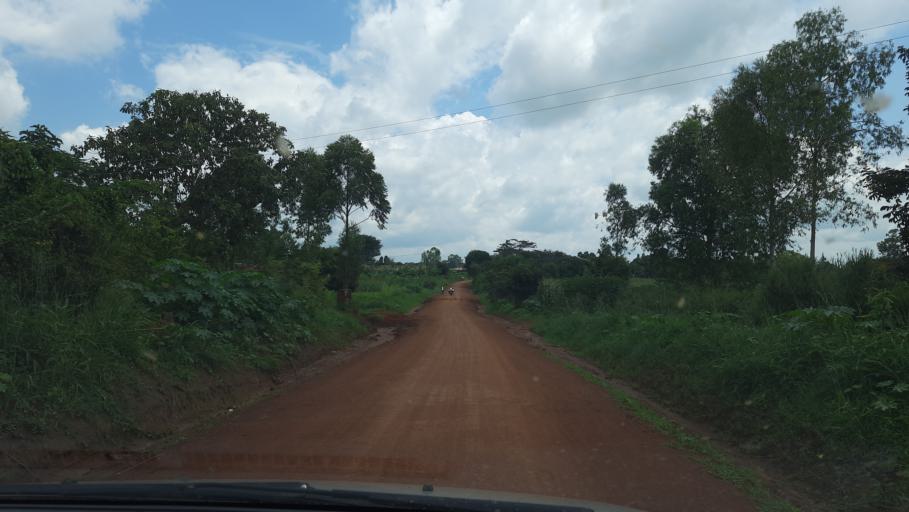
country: UG
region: Western Region
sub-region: Kiryandongo District
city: Kiryandongo
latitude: 1.8145
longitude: 31.9951
